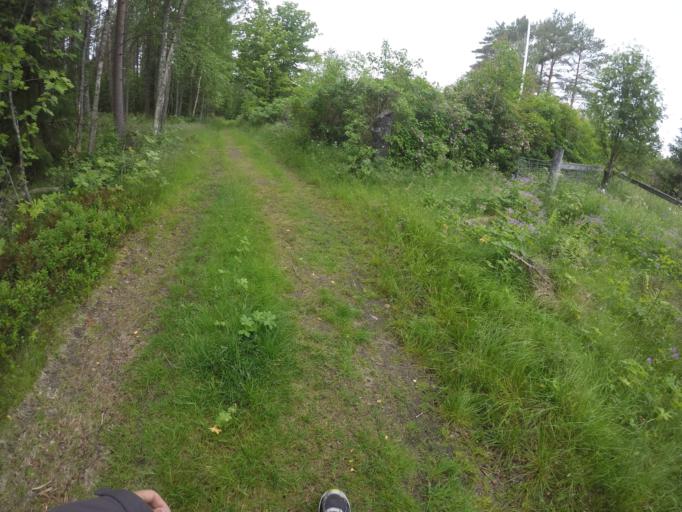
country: SE
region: Vaesternorrland
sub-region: Sundsvalls Kommun
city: Njurundabommen
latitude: 62.2223
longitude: 17.4927
